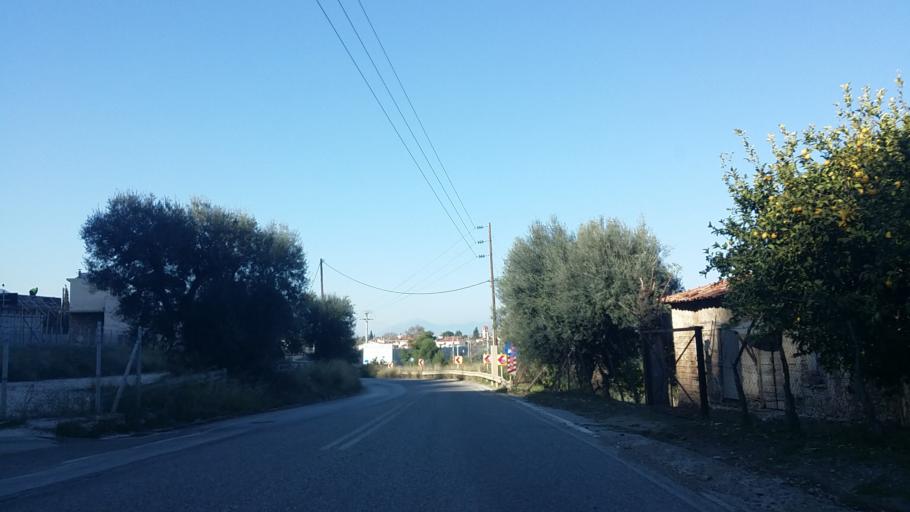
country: GR
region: West Greece
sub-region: Nomos Achaias
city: Temeni
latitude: 38.1818
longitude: 22.2094
